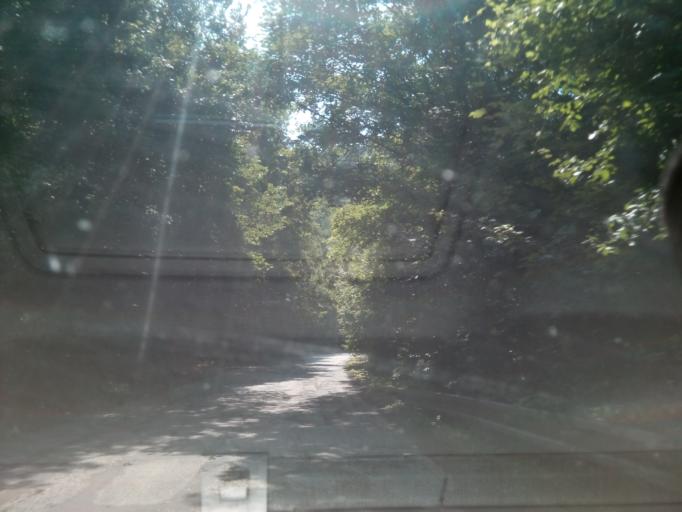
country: SK
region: Presovsky
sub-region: Okres Presov
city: Presov
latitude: 48.8602
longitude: 21.1975
